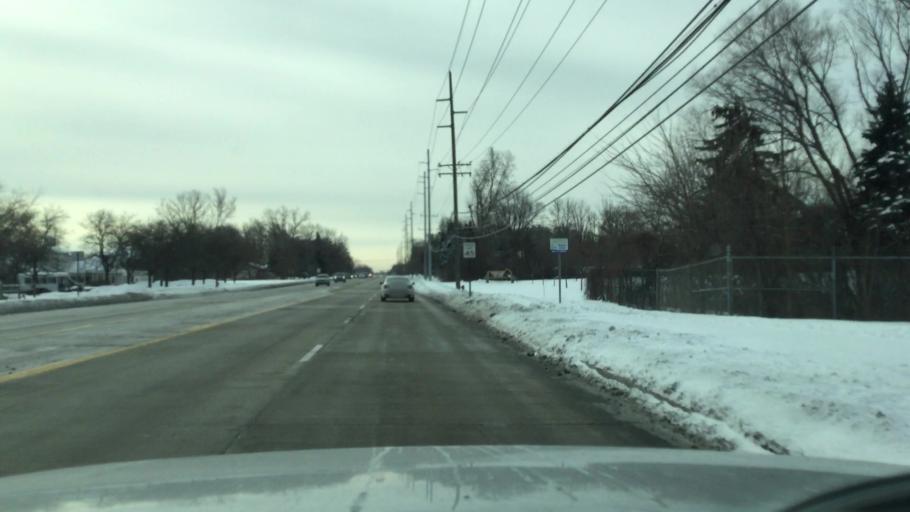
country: US
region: Michigan
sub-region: Oakland County
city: Troy
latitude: 42.6003
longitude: -83.1295
